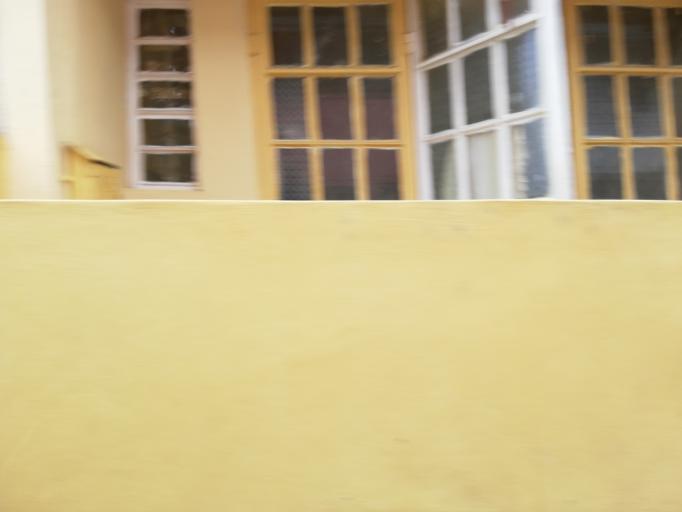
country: MU
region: Moka
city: Moka
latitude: -20.2139
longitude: 57.4680
